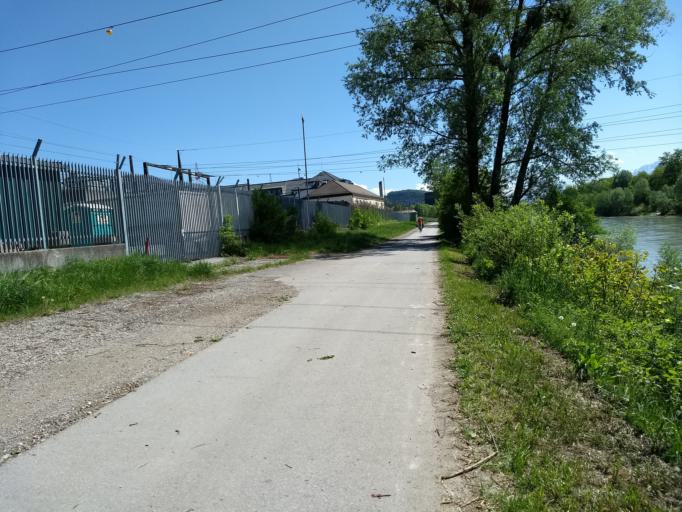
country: AT
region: Salzburg
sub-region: Politischer Bezirk Salzburg-Umgebung
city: Bergheim
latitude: 47.8332
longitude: 13.0270
